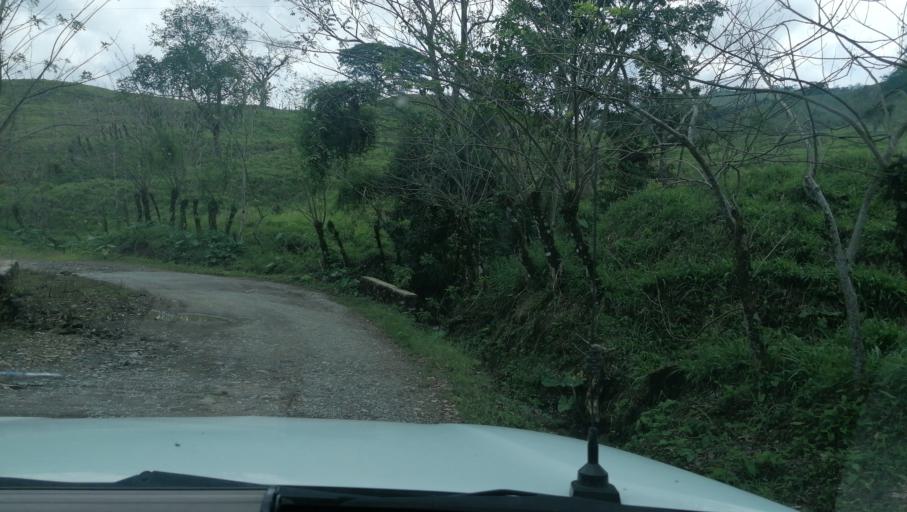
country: MX
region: Chiapas
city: Ixtacomitan
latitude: 17.4399
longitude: -93.2010
